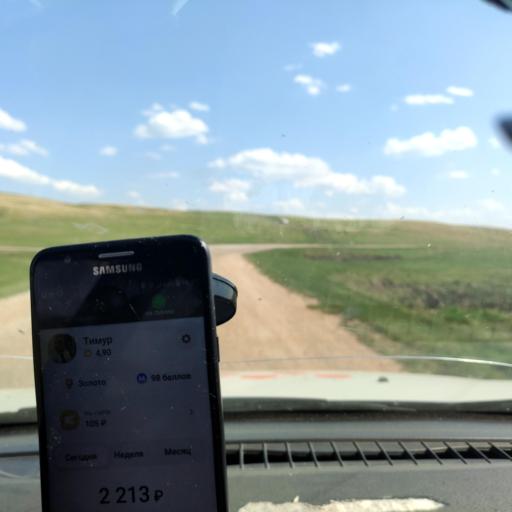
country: RU
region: Bashkortostan
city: Avdon
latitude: 54.5695
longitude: 55.6329
